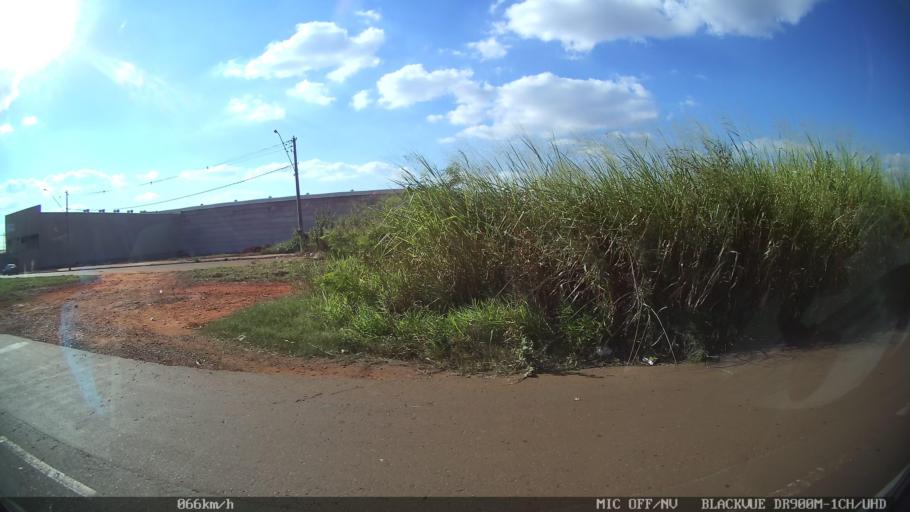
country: BR
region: Sao Paulo
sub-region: Santa Barbara D'Oeste
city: Santa Barbara d'Oeste
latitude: -22.7808
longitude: -47.3687
